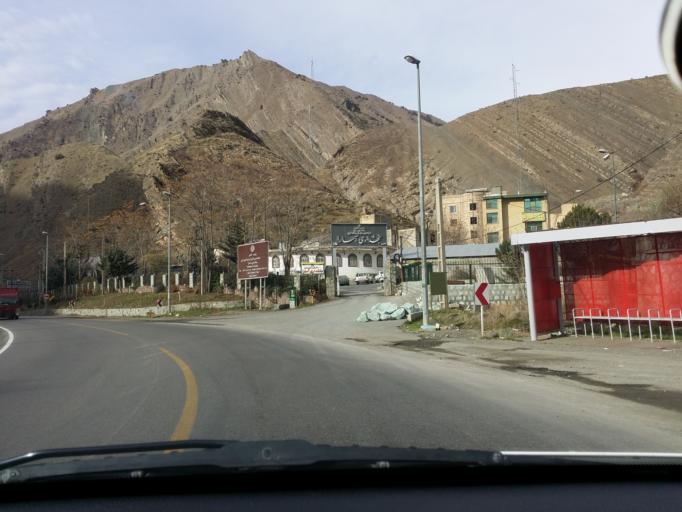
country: IR
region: Alborz
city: Karaj
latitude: 36.0408
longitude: 51.1862
